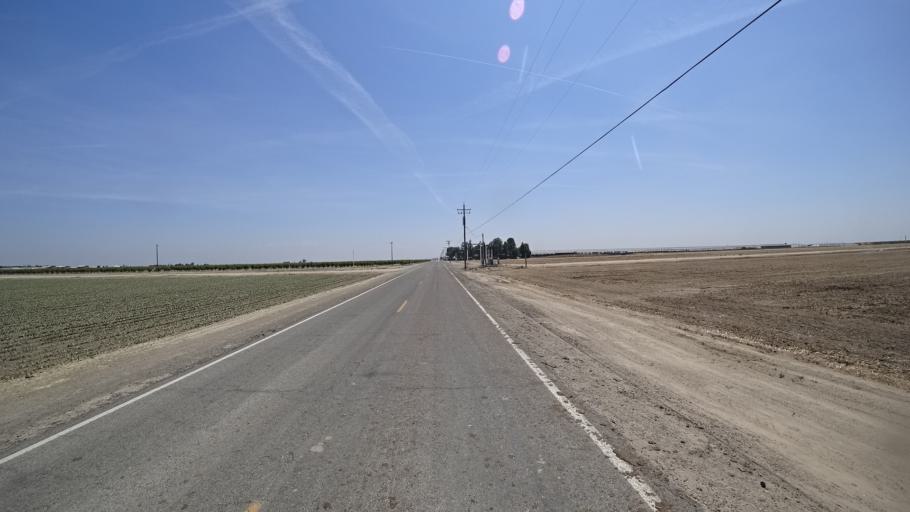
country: US
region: California
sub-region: Fresno County
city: Kingsburg
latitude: 36.4014
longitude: -119.5443
